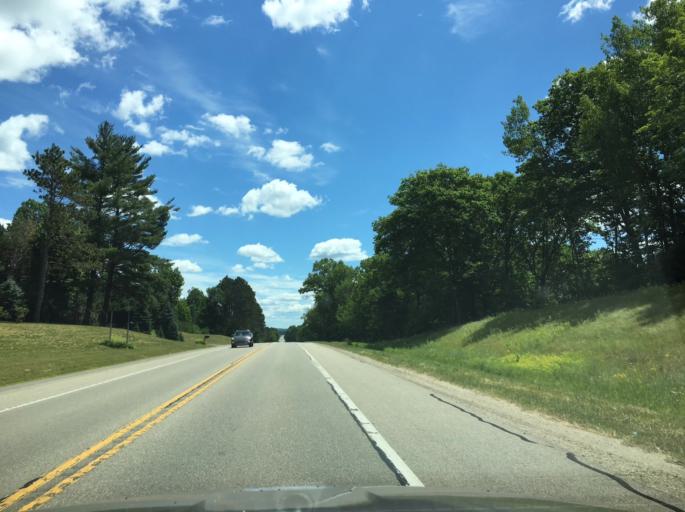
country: US
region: Michigan
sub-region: Osceola County
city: Reed City
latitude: 43.8724
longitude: -85.4420
